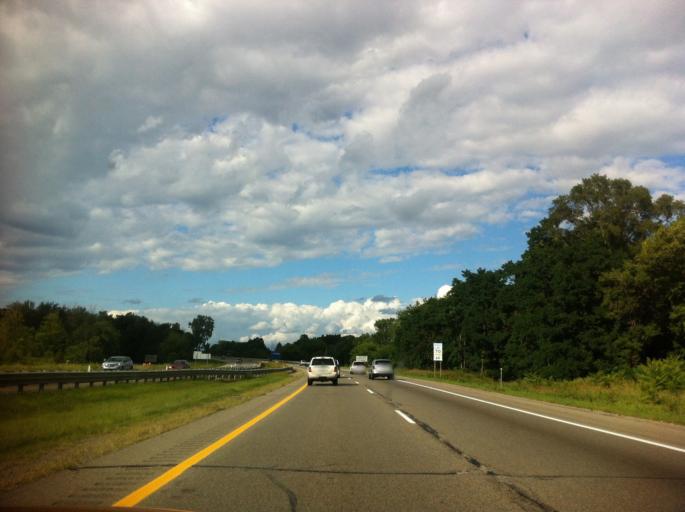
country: US
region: Michigan
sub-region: Livingston County
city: Whitmore Lake
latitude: 42.4351
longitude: -83.7598
